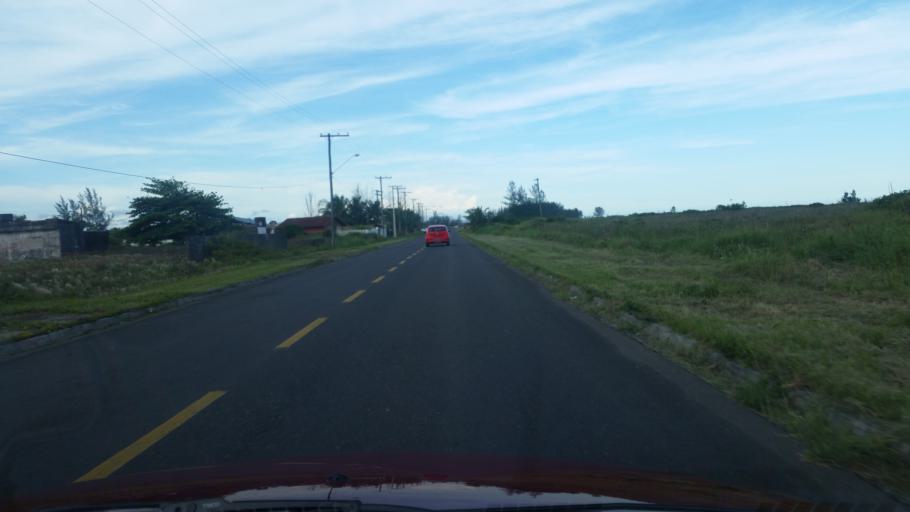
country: BR
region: Sao Paulo
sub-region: Iguape
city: Iguape
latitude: -24.7896
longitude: -47.6141
